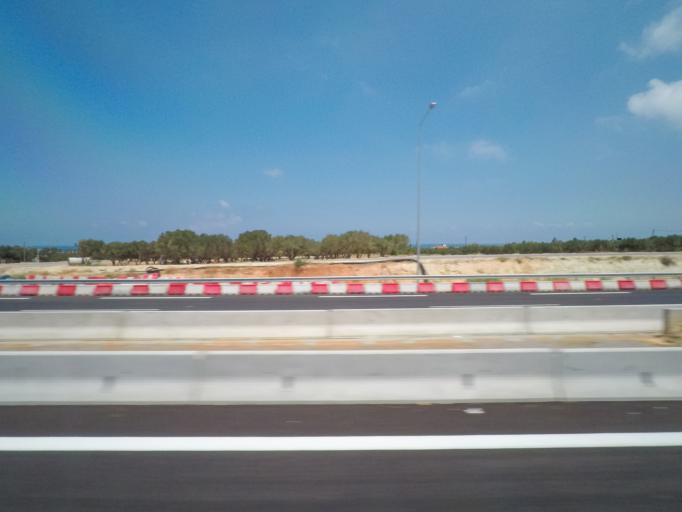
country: GR
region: Crete
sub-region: Nomos Irakleiou
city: Gournes
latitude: 35.3239
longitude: 25.2936
